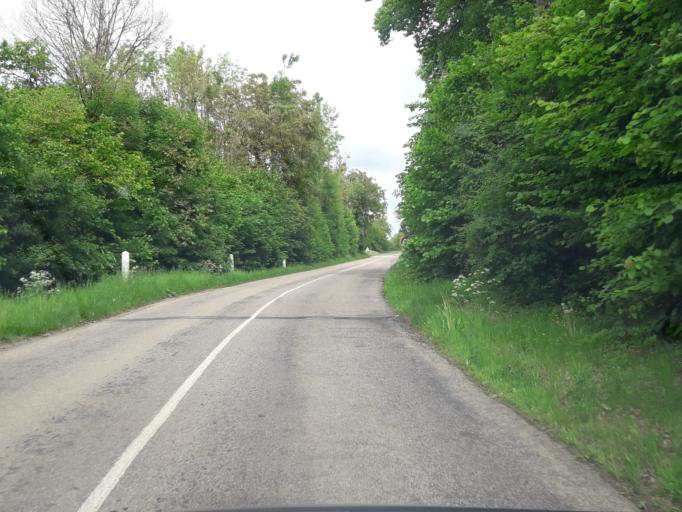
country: FR
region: Ile-de-France
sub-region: Departement de l'Essonne
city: Saclas
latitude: 48.3594
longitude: 2.1611
